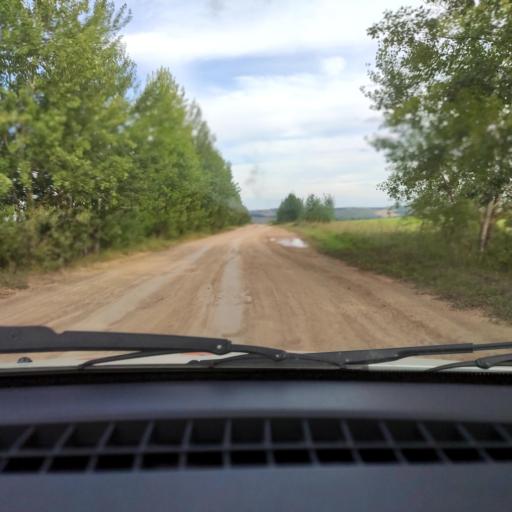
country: RU
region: Bashkortostan
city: Blagoveshchensk
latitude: 55.0989
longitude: 55.8100
